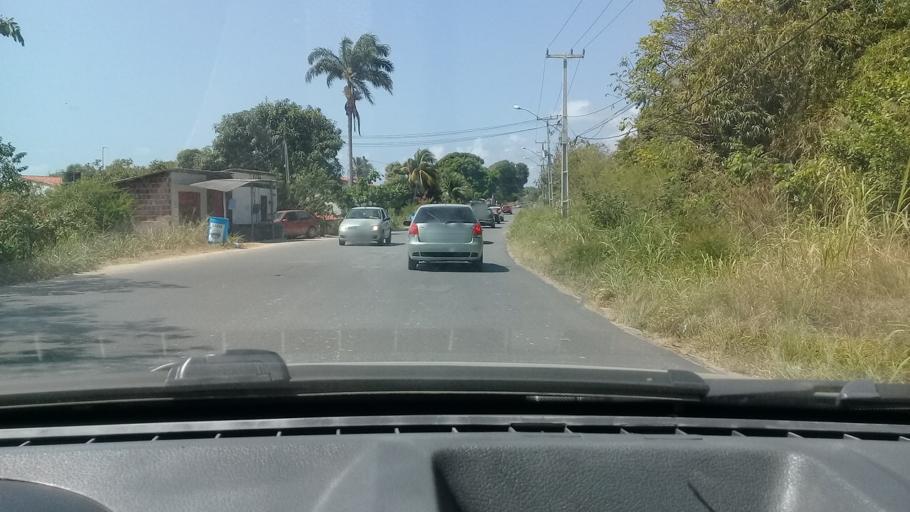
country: BR
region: Pernambuco
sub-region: Itamaraca
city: Itamaraca
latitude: -7.7778
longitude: -34.8356
